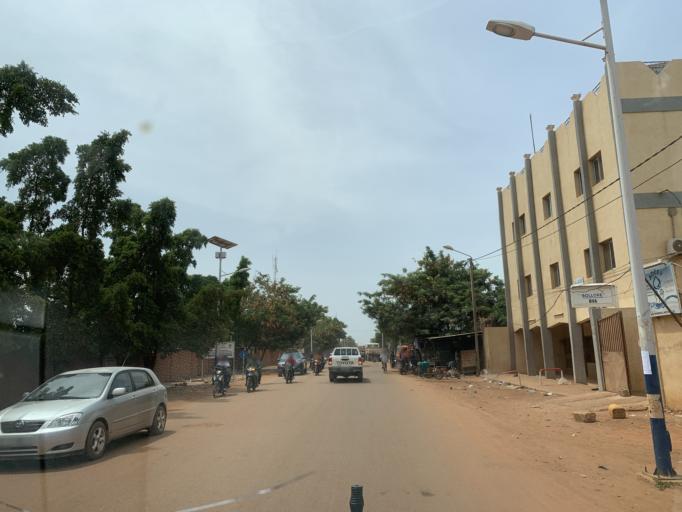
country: BF
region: Centre
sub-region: Kadiogo Province
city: Ouagadougou
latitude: 12.3355
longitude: -1.4981
